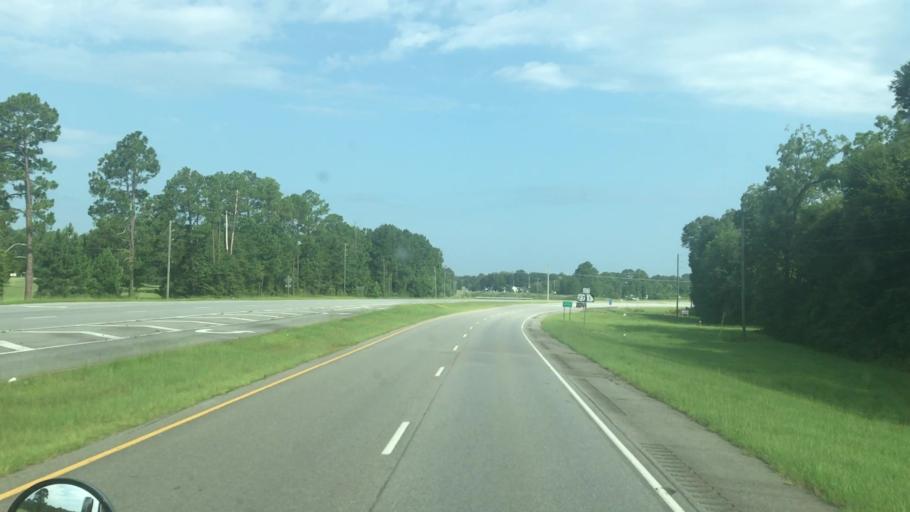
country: US
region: Georgia
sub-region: Early County
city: Blakely
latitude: 31.3546
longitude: -84.9210
